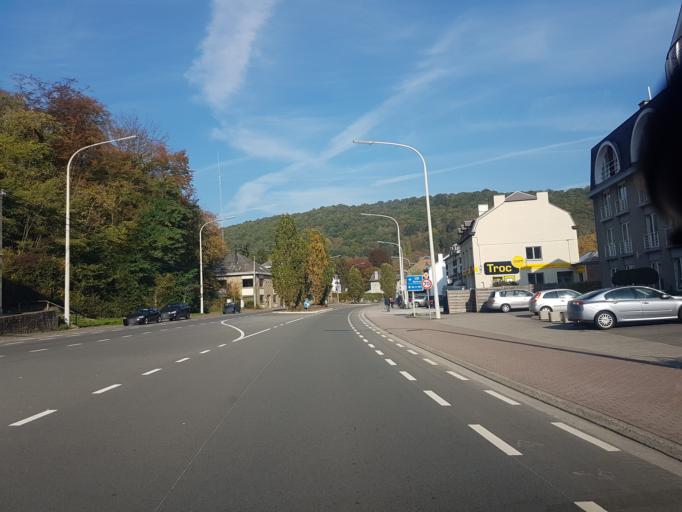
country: BE
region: Wallonia
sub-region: Province de Namur
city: Profondeville
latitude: 50.3794
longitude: 4.8668
